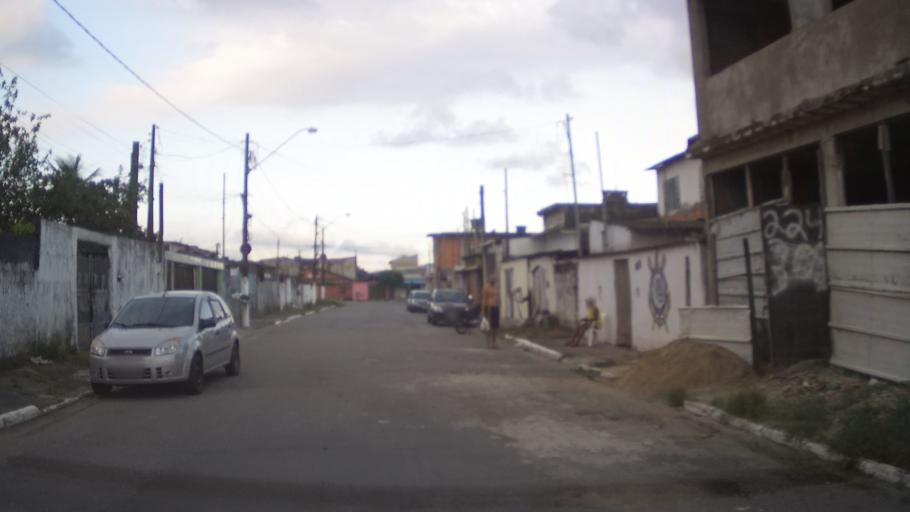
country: BR
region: Sao Paulo
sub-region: Praia Grande
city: Praia Grande
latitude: -24.0085
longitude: -46.4447
